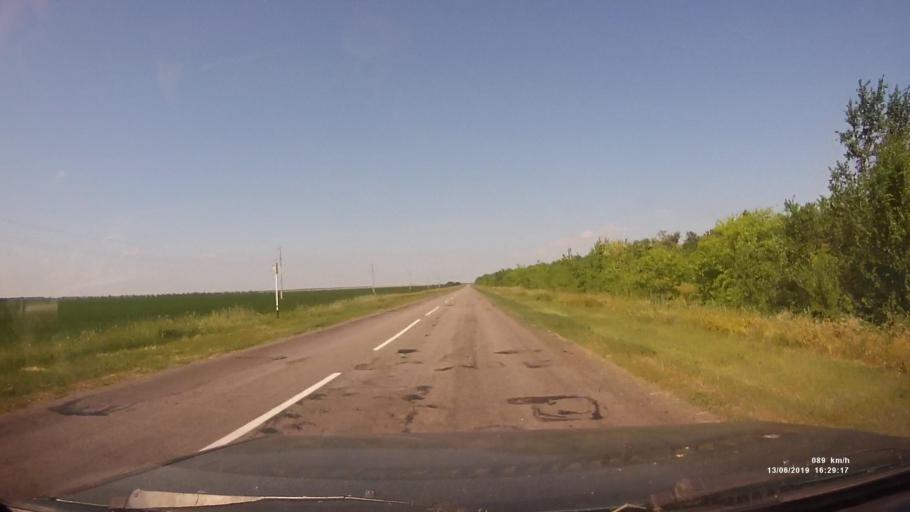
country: RU
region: Rostov
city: Kazanskaya
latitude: 49.8287
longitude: 41.2144
